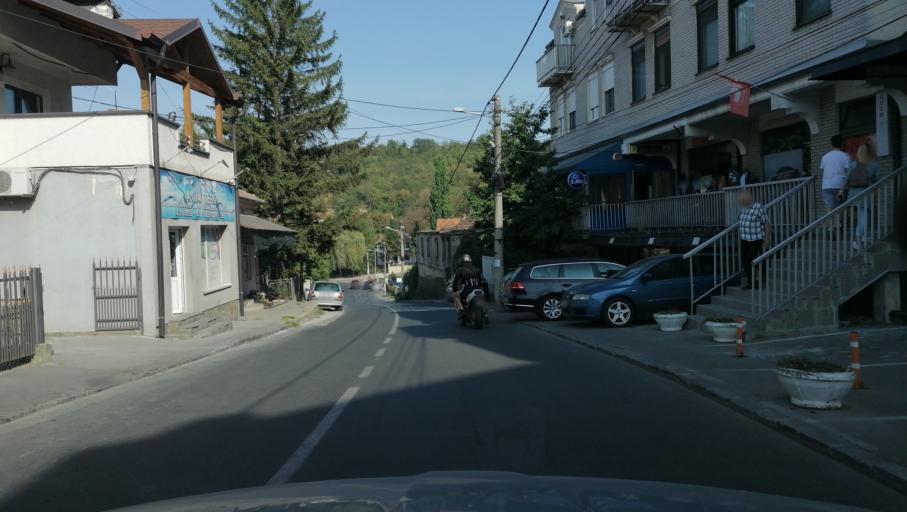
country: RS
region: Central Serbia
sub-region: Belgrade
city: Grocka
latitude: 44.6633
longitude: 20.5925
